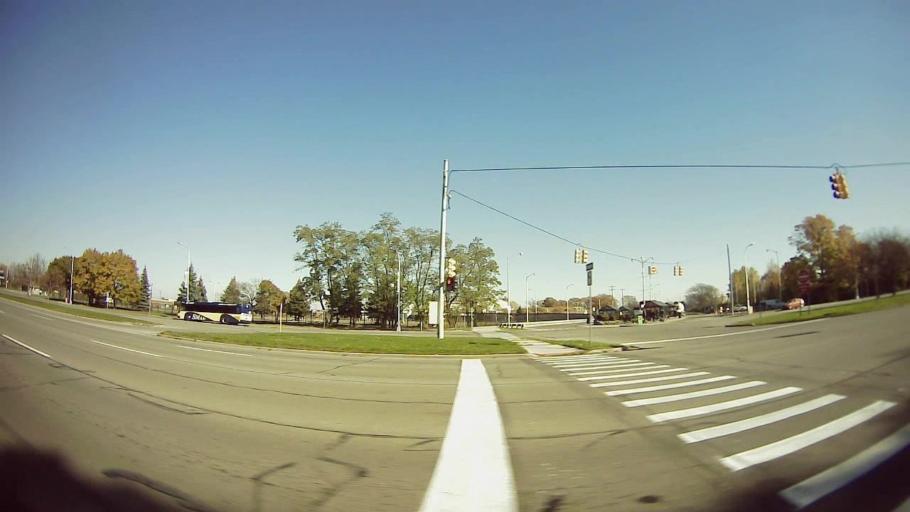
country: US
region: Michigan
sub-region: Oakland County
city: Ferndale
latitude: 42.4413
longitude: -83.1218
